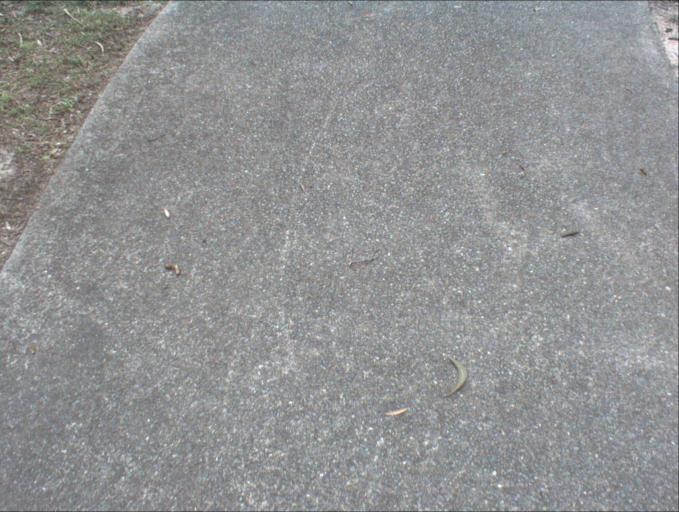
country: AU
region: Queensland
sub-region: Logan
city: Park Ridge South
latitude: -27.6982
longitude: 153.0312
